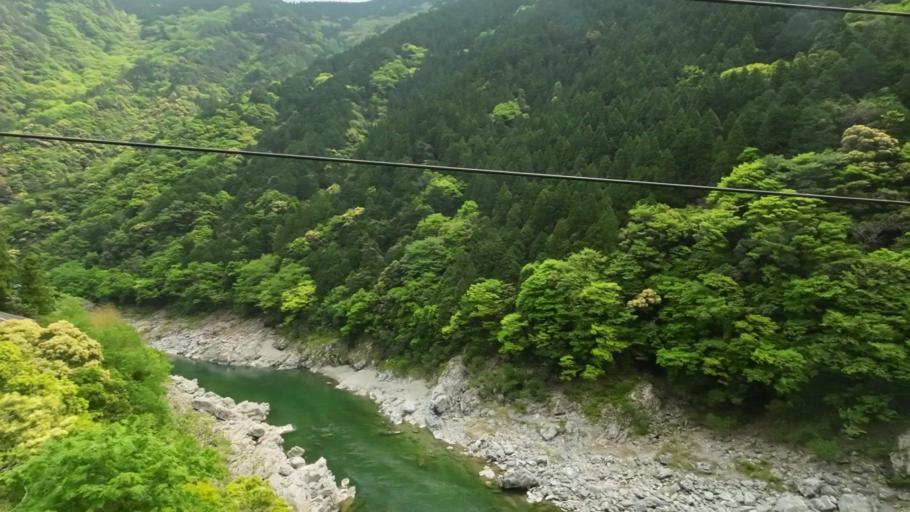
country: JP
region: Tokushima
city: Ikedacho
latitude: 33.9113
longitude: 133.7574
